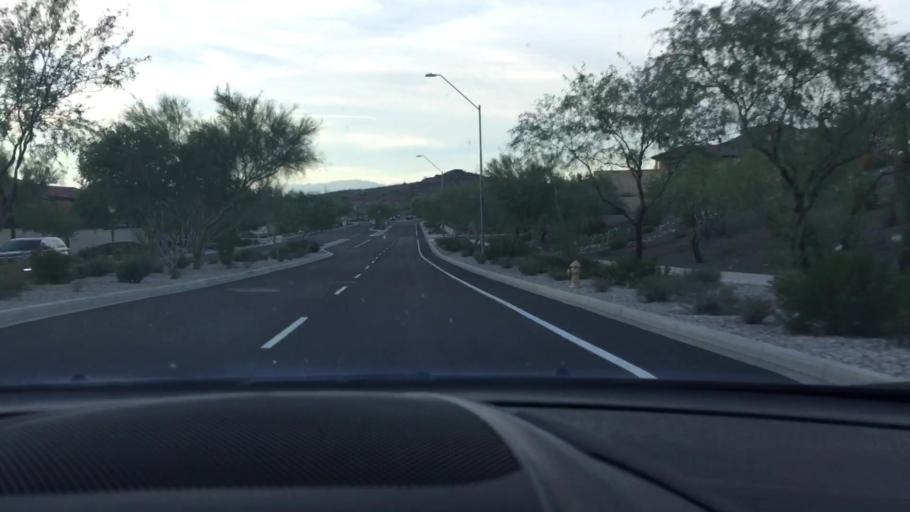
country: US
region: Arizona
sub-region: Maricopa County
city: Sun City West
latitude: 33.7153
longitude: -112.2851
